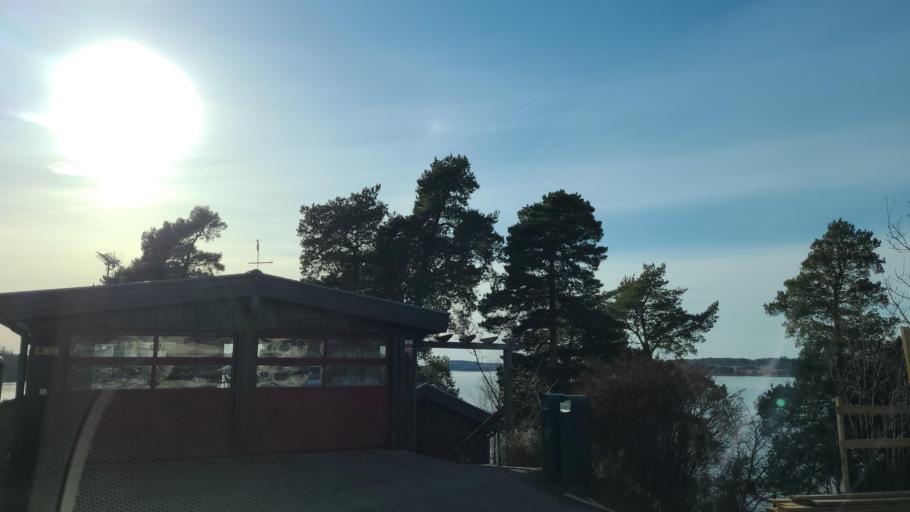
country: SE
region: Stockholm
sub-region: Ekero Kommun
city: Ekeroe
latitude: 59.2638
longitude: 17.7765
